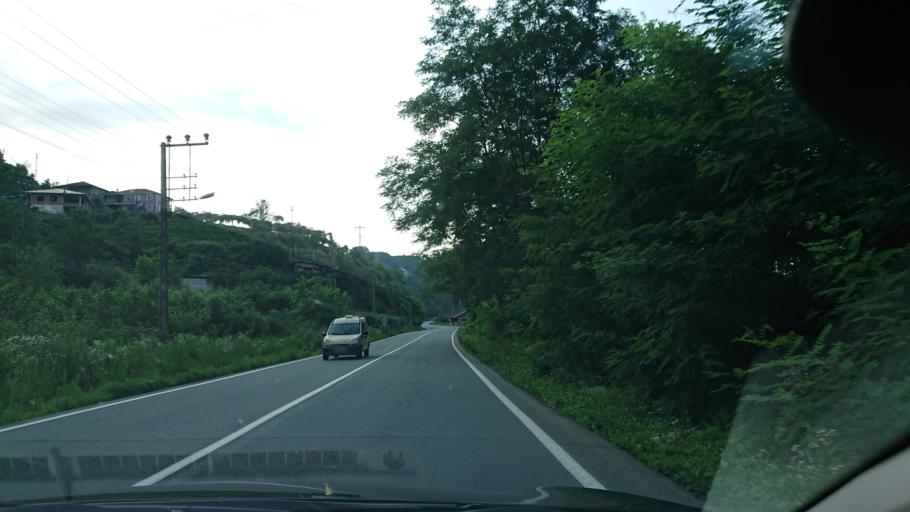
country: TR
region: Rize
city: Cayeli
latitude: 41.0646
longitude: 40.7155
